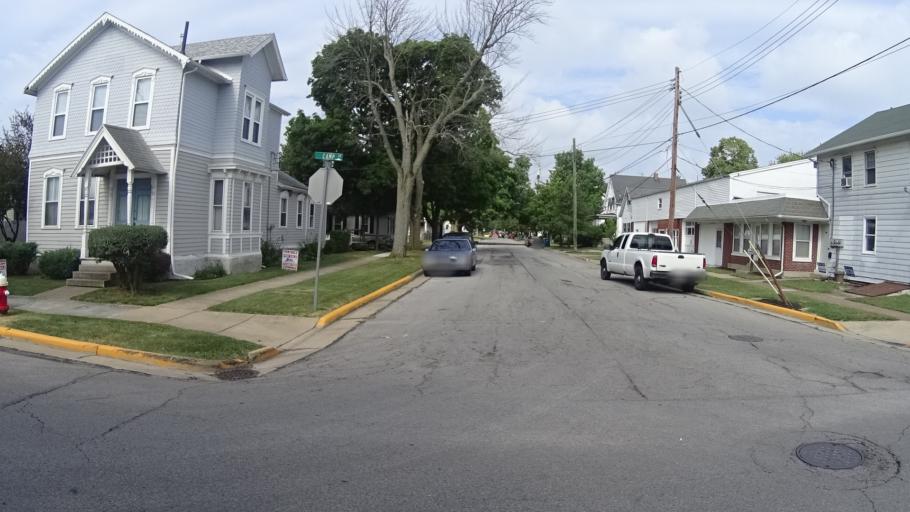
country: US
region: Ohio
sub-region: Erie County
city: Sandusky
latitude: 41.4440
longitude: -82.7203
